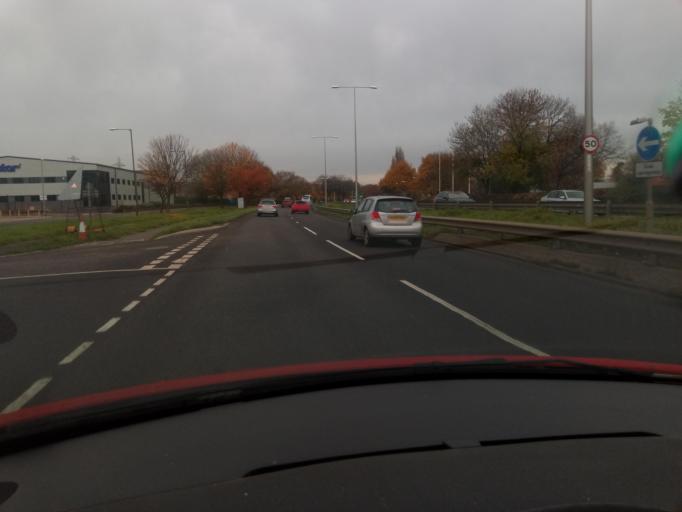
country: GB
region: England
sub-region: Derbyshire
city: Borrowash
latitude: 52.9087
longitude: -1.4307
